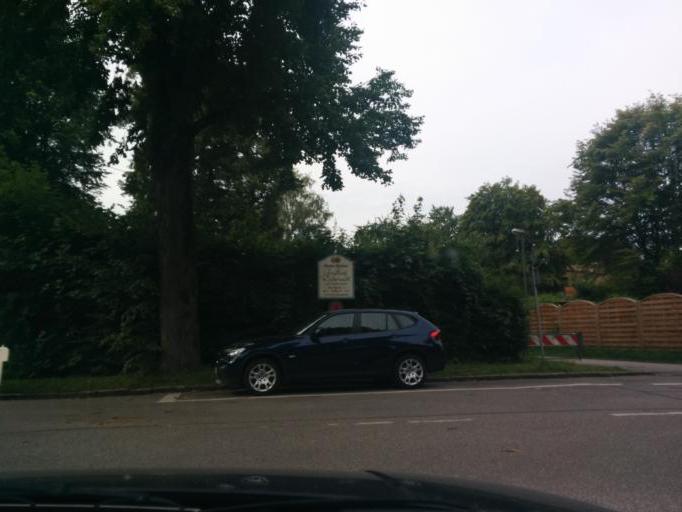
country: DE
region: Bavaria
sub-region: Upper Bavaria
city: Pullach im Isartal
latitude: 48.0823
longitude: 11.5369
